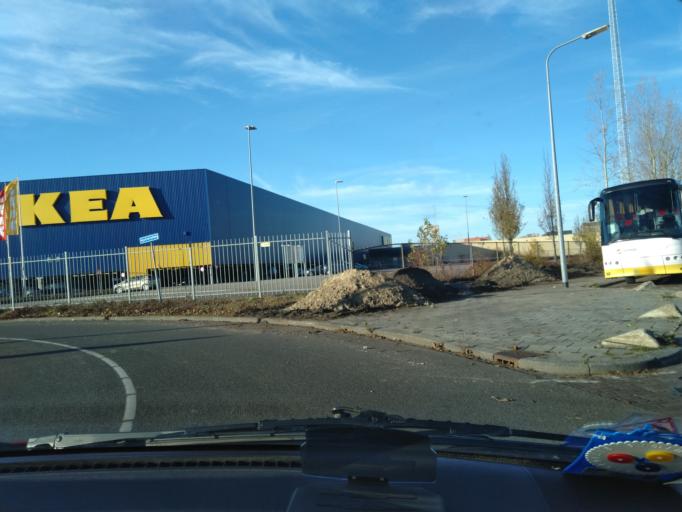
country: NL
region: Groningen
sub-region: Gemeente Groningen
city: Oosterpark
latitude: 53.2160
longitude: 6.5921
